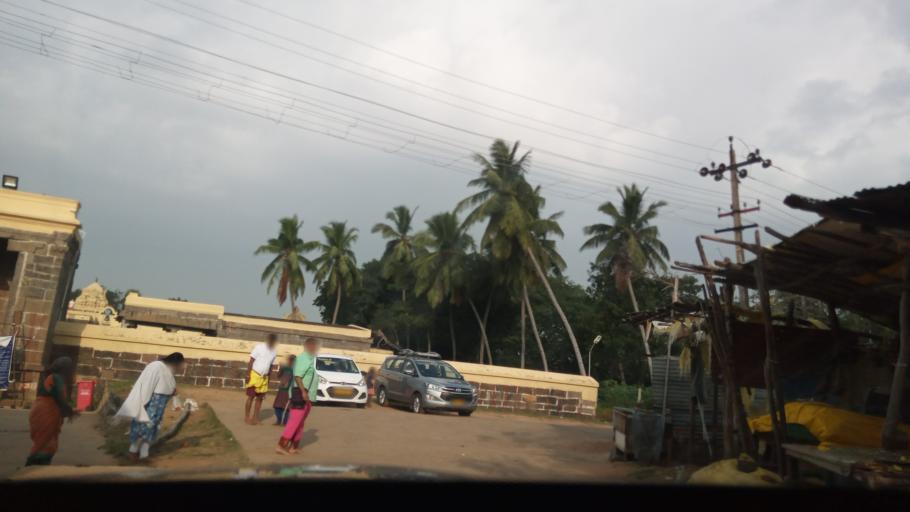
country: IN
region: Tamil Nadu
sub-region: Kancheepuram
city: Mamallapuram
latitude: 12.7632
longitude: 80.2427
